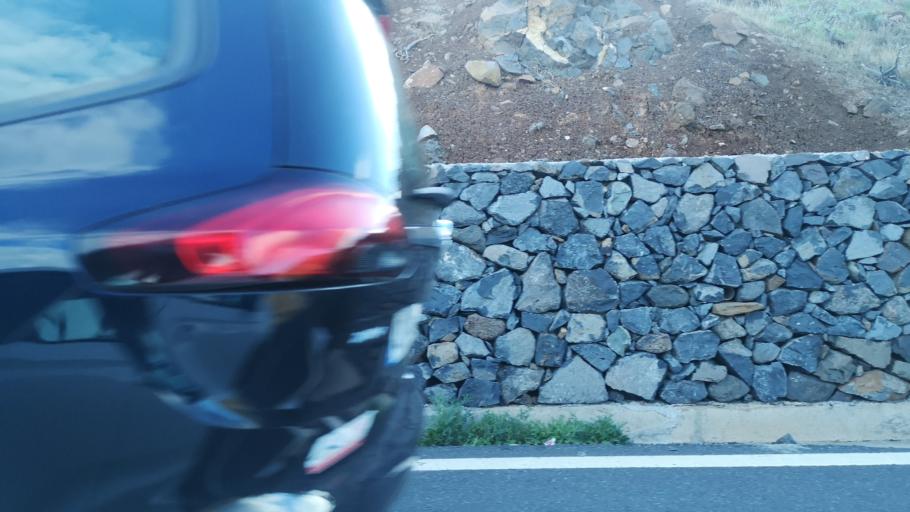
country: ES
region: Canary Islands
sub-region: Provincia de Santa Cruz de Tenerife
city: San Sebastian de la Gomera
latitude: 28.0846
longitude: -17.1332
